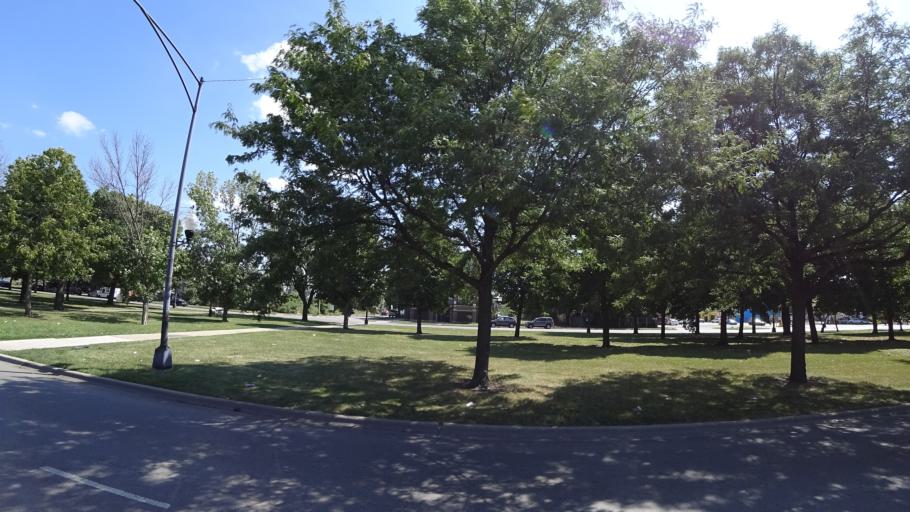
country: US
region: Illinois
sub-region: Cook County
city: Cicero
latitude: 41.8670
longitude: -87.7202
